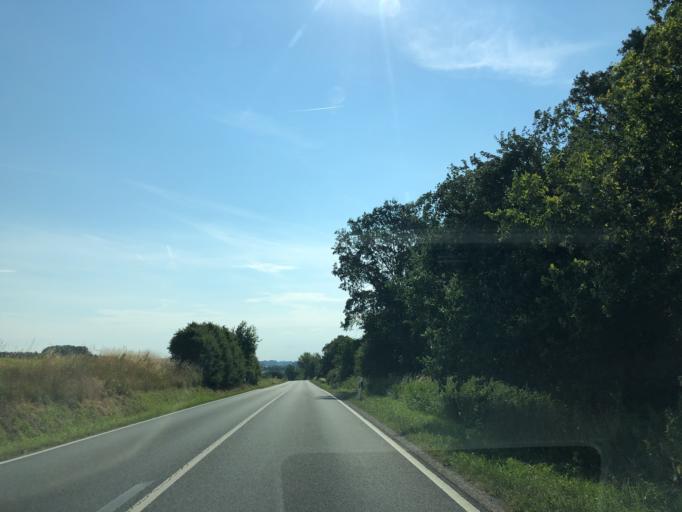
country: DE
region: Bavaria
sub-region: Regierungsbezirk Unterfranken
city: Geiselwind
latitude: 49.7707
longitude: 10.4997
